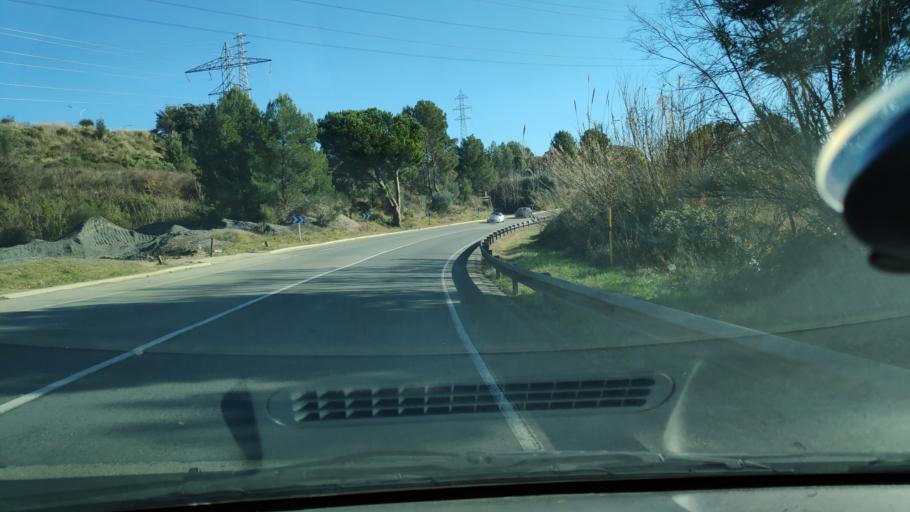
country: ES
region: Catalonia
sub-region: Provincia de Barcelona
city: Terrassa
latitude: 41.5559
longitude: 2.0498
